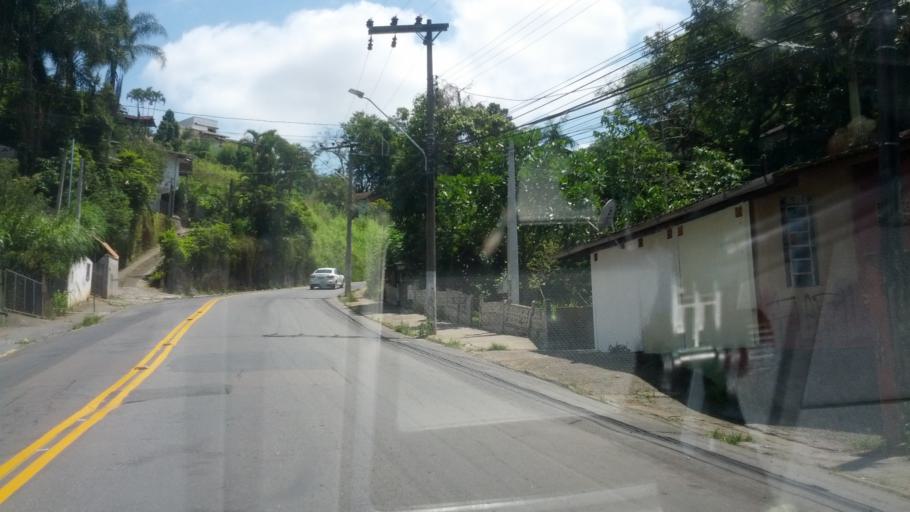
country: BR
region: Santa Catarina
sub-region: Blumenau
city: Blumenau
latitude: -26.9100
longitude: -49.0930
